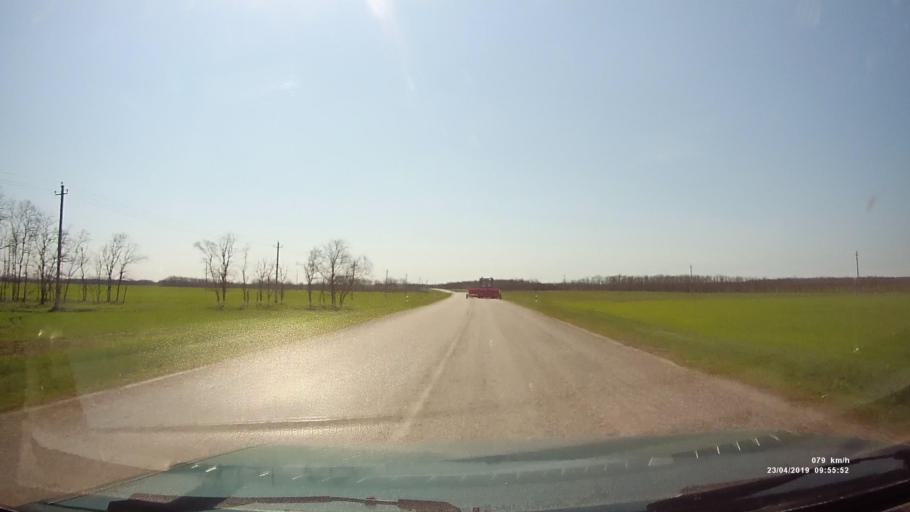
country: RU
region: Rostov
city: Orlovskiy
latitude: 46.8036
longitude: 42.0662
